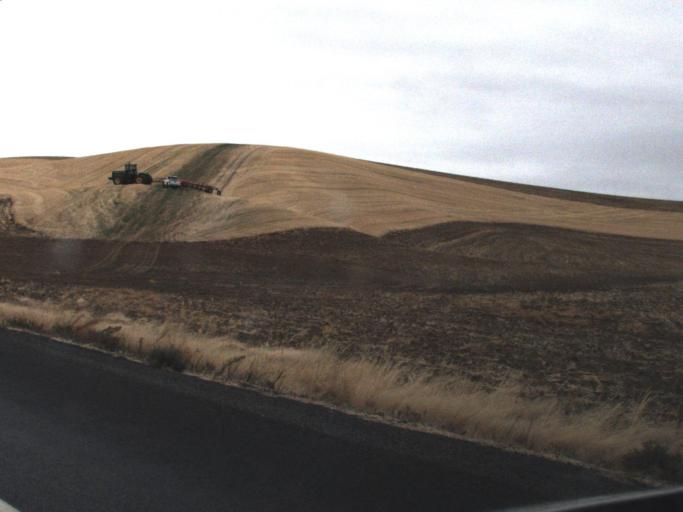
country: US
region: Washington
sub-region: Whitman County
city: Pullman
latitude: 46.7596
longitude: -117.2469
